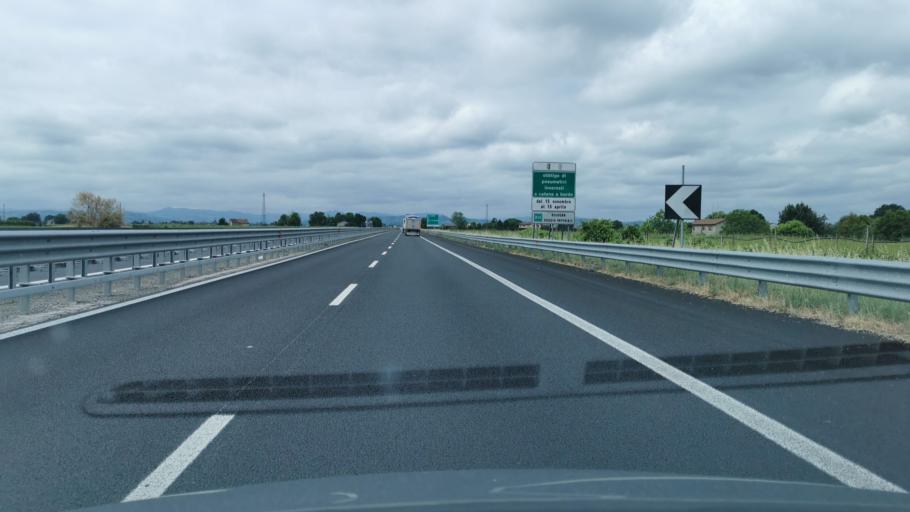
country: IT
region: Emilia-Romagna
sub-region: Provincia di Ravenna
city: Solarolo
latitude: 44.3649
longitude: 11.8288
